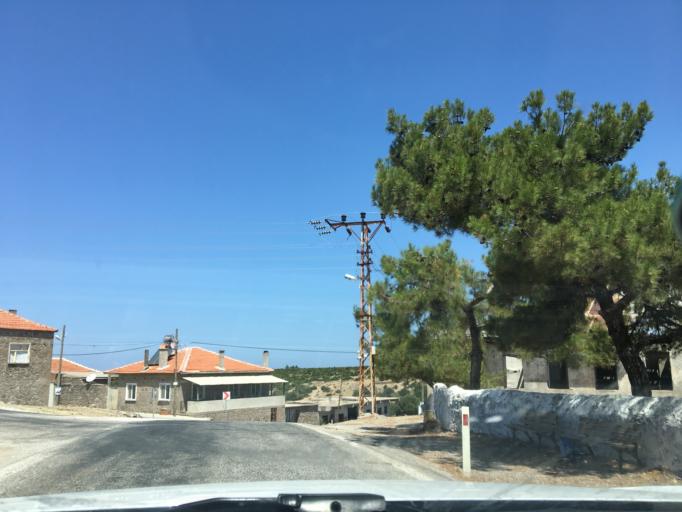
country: TR
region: Canakkale
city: Gulpinar
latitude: 39.5021
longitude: 26.1374
